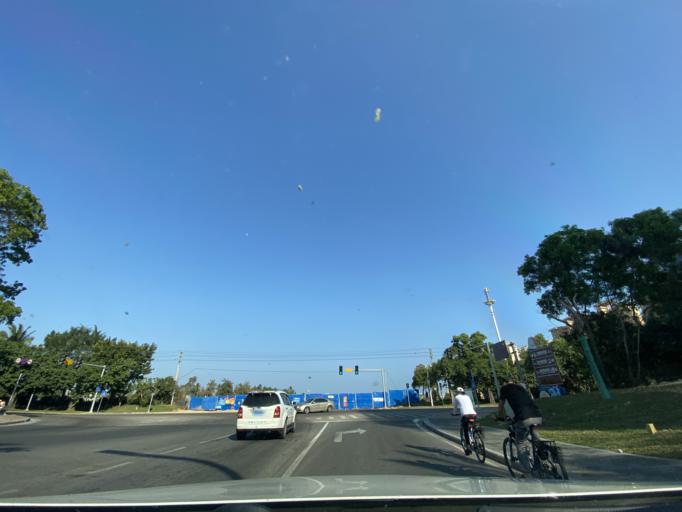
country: CN
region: Hainan
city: Xincun
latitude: 18.4235
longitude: 109.9606
